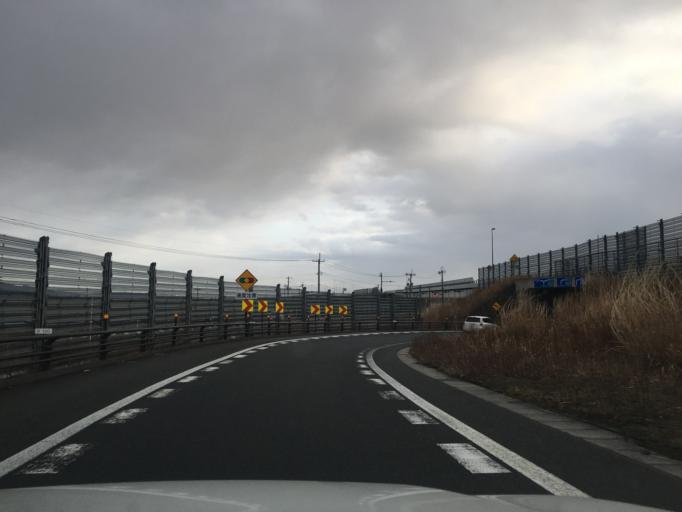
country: JP
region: Yamagata
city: Tsuruoka
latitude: 38.7161
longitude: 139.7573
